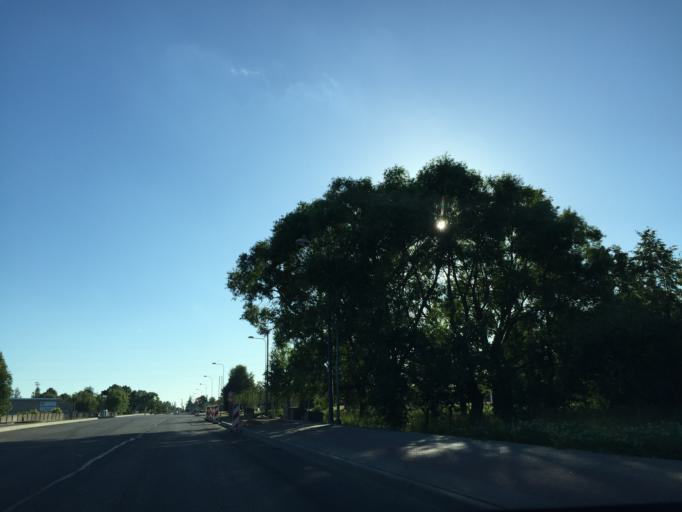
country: LV
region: Ventspils
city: Ventspils
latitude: 57.3976
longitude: 21.6284
